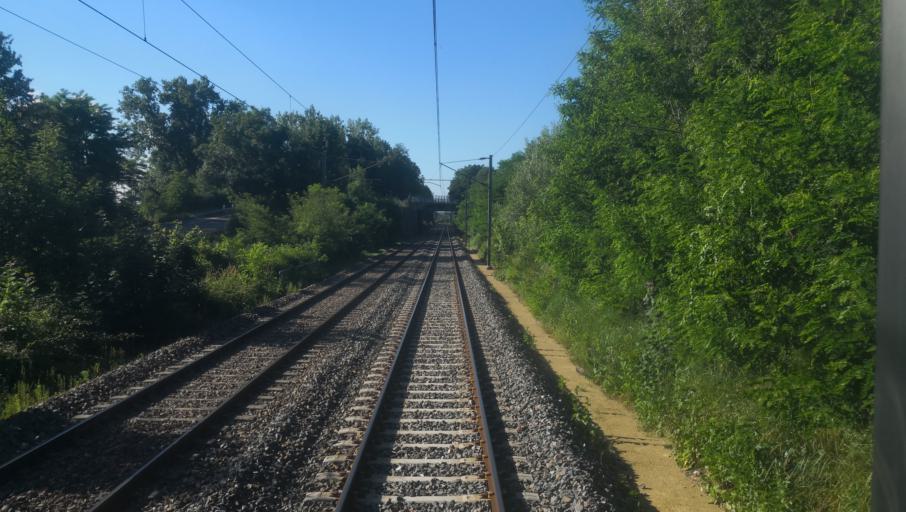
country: FR
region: Bourgogne
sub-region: Departement de la Nievre
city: Cosne-Cours-sur-Loire
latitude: 47.4403
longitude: 2.9333
